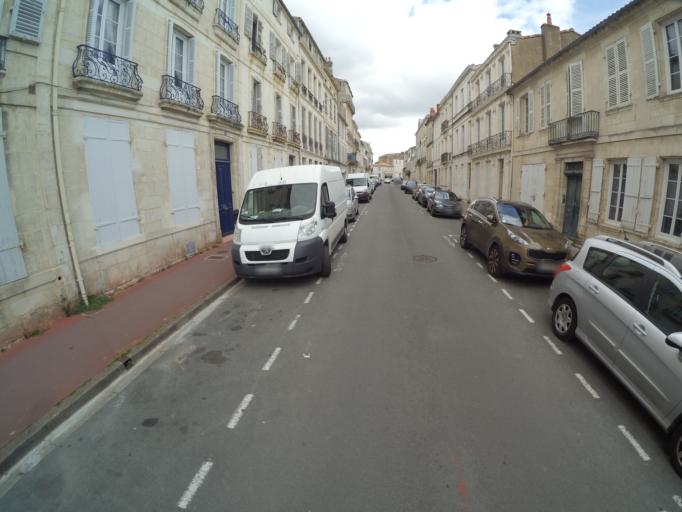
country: FR
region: Poitou-Charentes
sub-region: Departement de la Charente-Maritime
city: Rochefort
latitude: 45.9388
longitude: -0.9606
